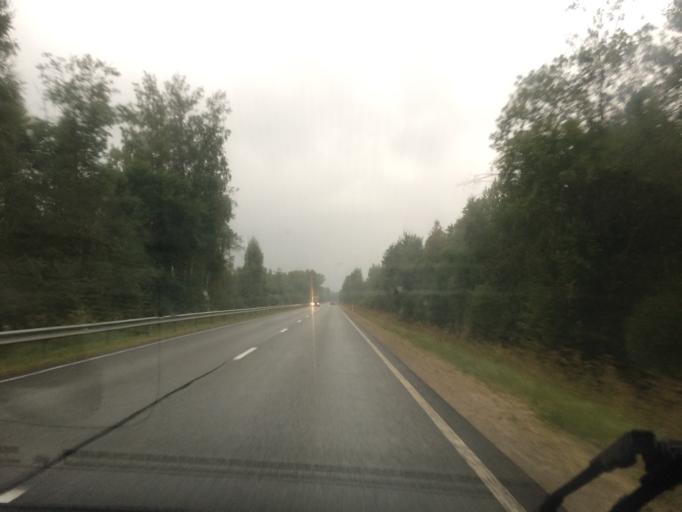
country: LV
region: Livani
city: Livani
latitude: 56.5291
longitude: 26.3849
